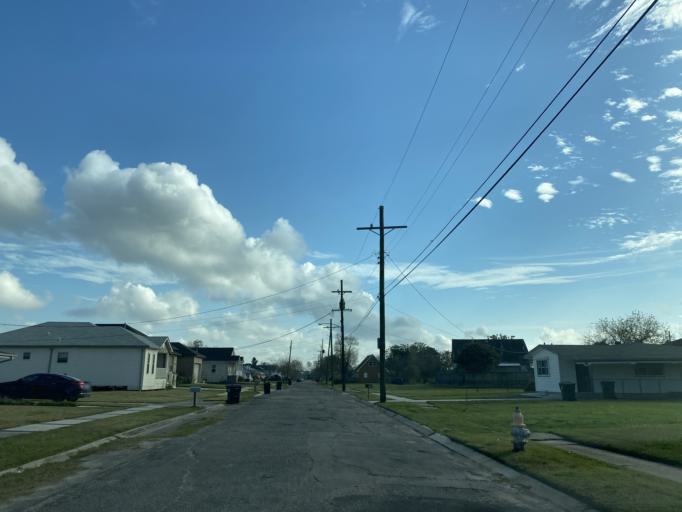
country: US
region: Louisiana
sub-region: Saint Bernard Parish
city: Arabi
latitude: 30.0279
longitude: -90.0374
